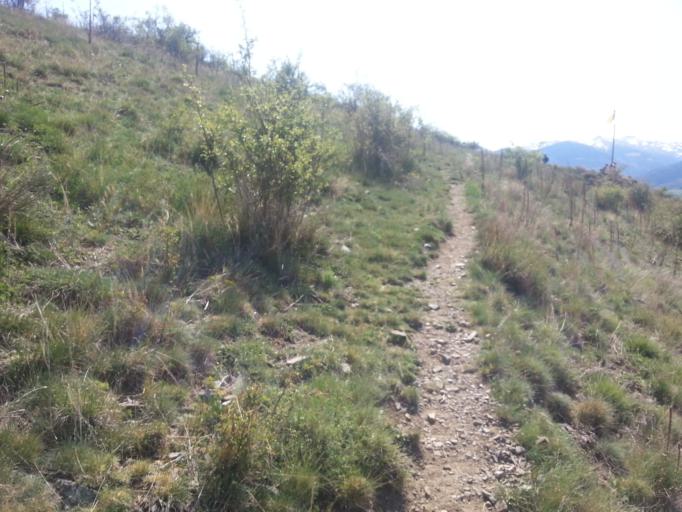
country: ES
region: Catalonia
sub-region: Provincia de Girona
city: Llivia
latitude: 42.4662
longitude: 1.9852
